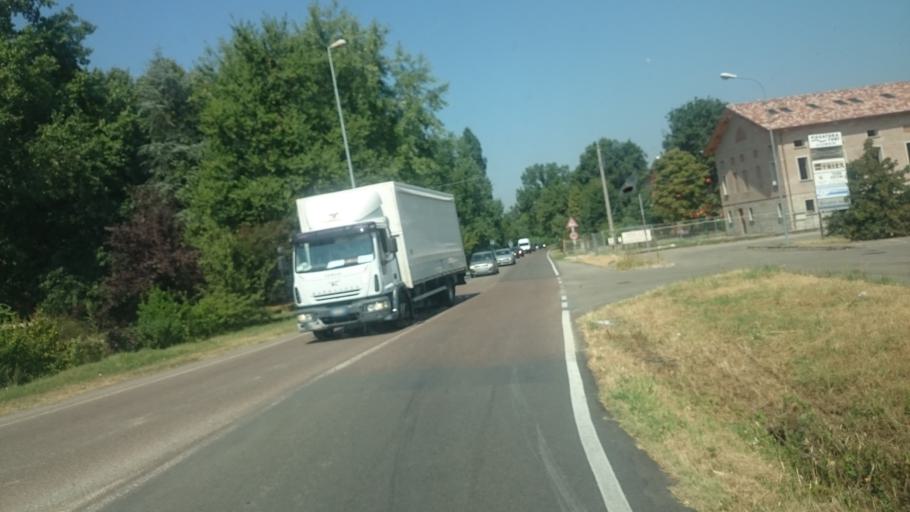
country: IT
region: Emilia-Romagna
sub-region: Provincia di Reggio Emilia
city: Arceto
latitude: 44.6247
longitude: 10.7151
